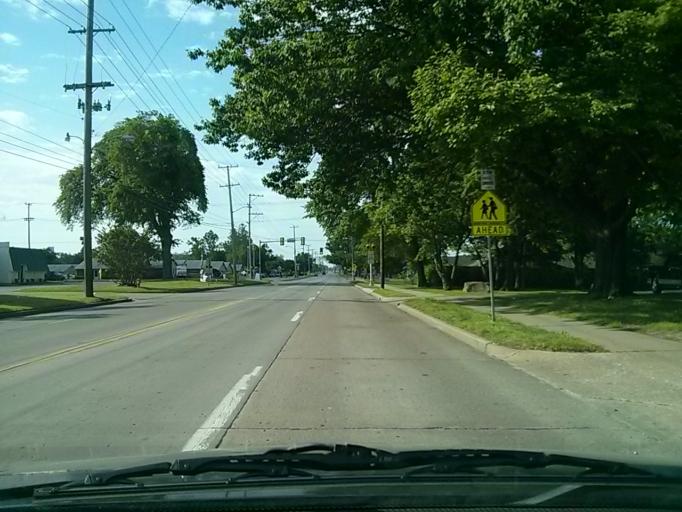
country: US
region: Oklahoma
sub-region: Tulsa County
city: Jenks
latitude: 36.0835
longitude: -95.9758
